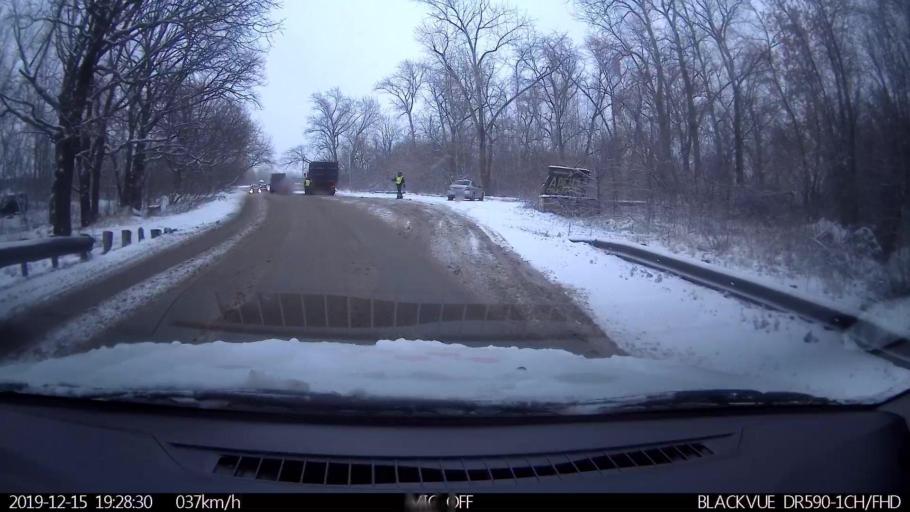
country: RU
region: Nizjnij Novgorod
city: Neklyudovo
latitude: 56.3575
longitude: 43.8909
